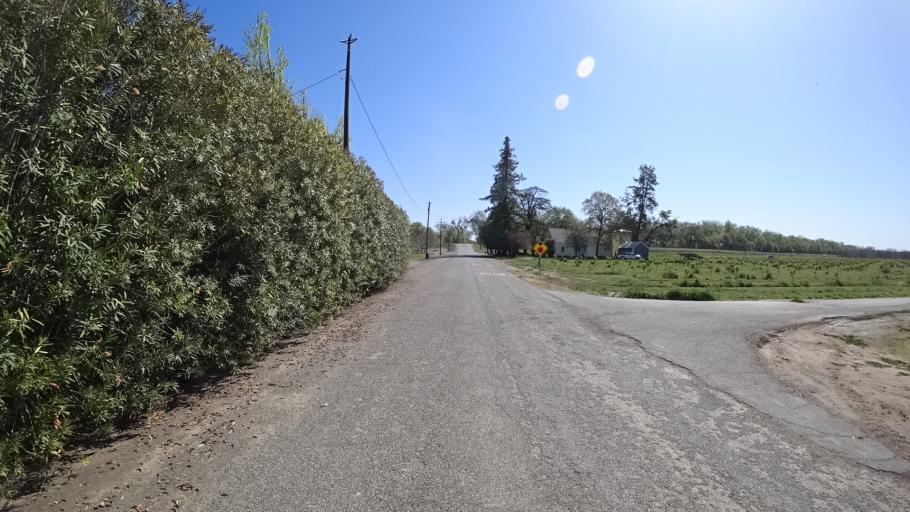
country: US
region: California
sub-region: Glenn County
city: Willows
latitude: 39.4501
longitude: -122.0200
